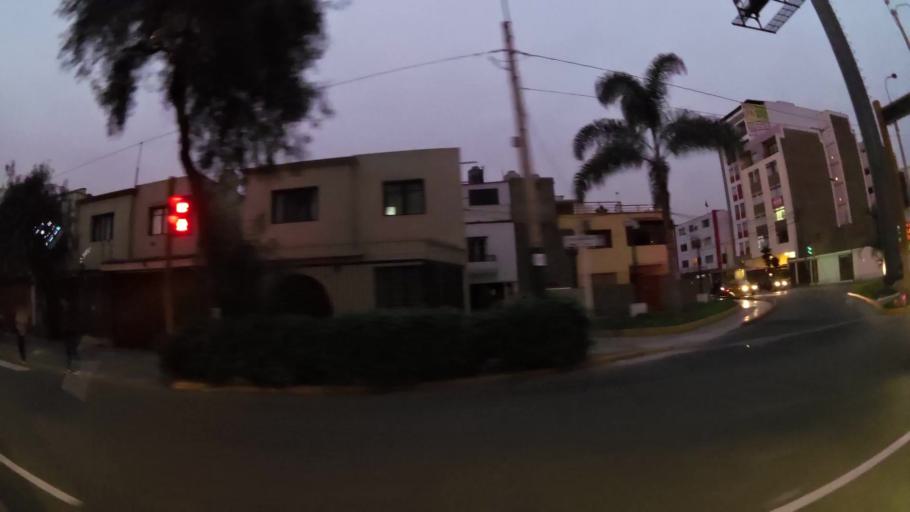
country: PE
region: Lima
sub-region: Lima
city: Surco
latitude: -12.1392
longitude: -77.0223
